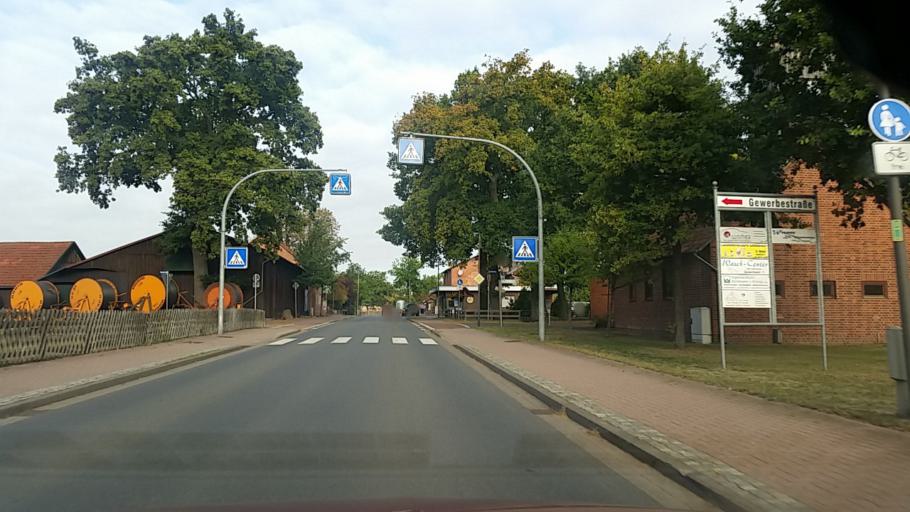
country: DE
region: Lower Saxony
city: Ahnsbeck
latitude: 52.6079
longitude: 10.2888
